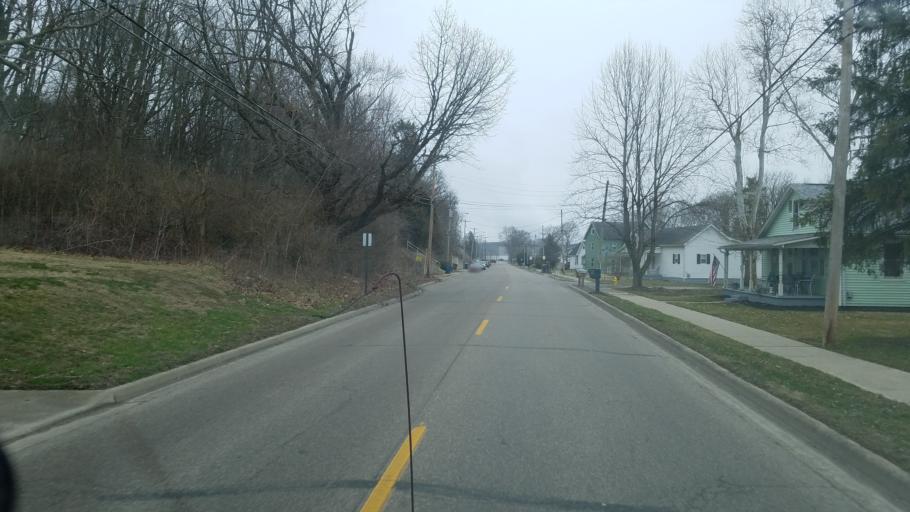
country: US
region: Indiana
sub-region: Wabash County
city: Wabash
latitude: 40.7968
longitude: -85.8373
